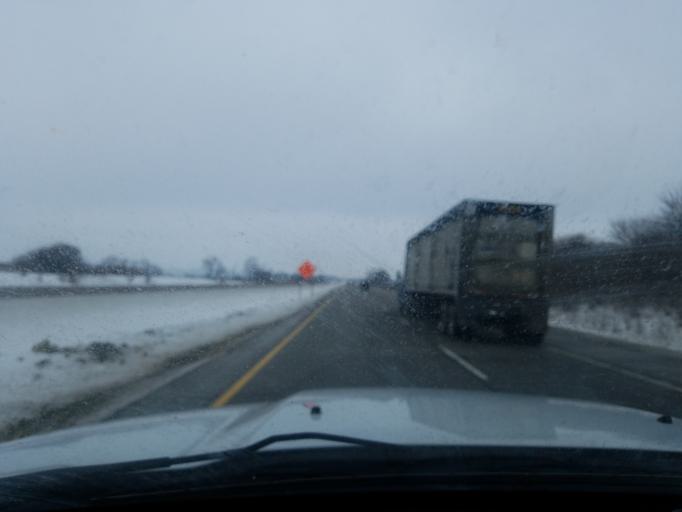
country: US
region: Indiana
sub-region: Marshall County
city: Argos
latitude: 41.2179
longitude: -86.2609
